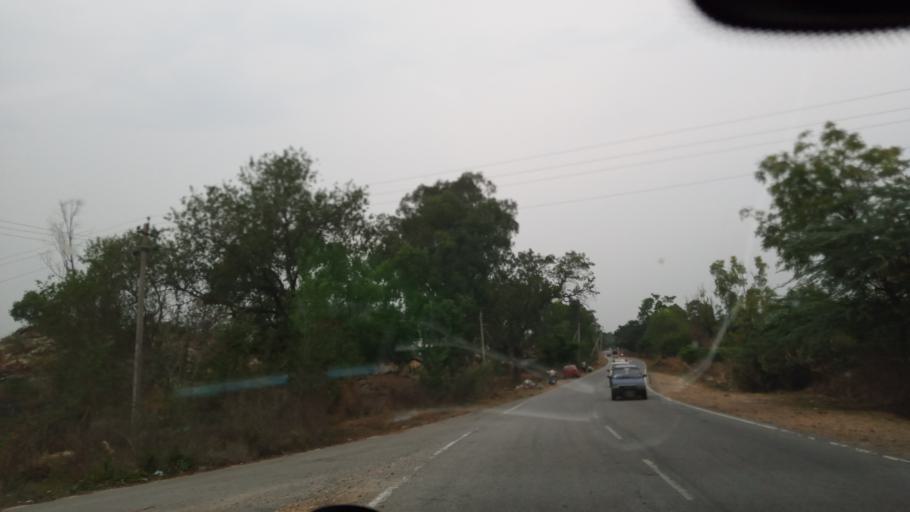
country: IN
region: Karnataka
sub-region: Mandya
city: Belluru
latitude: 12.9486
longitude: 76.7517
